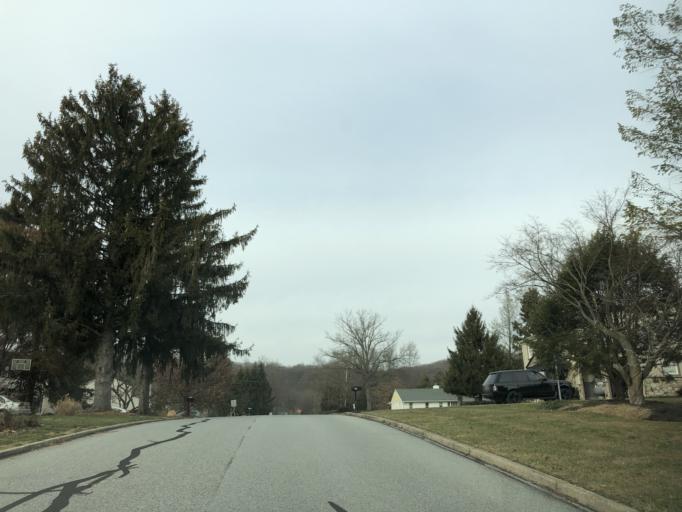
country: US
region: Pennsylvania
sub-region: Chester County
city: Exton
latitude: 40.0329
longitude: -75.6446
